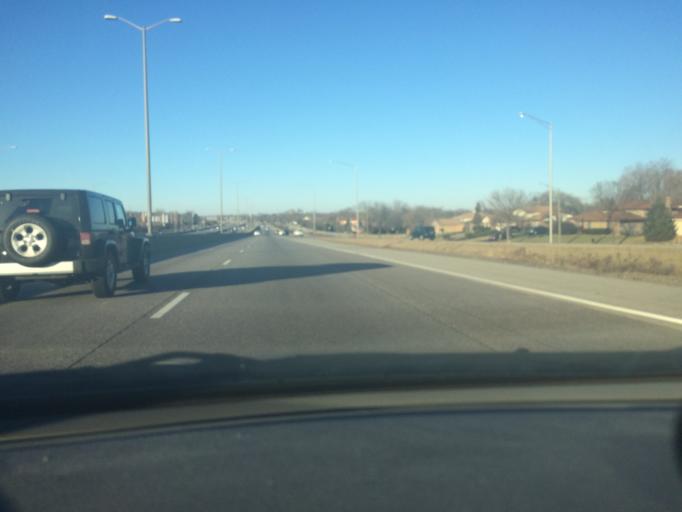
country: US
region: Illinois
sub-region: Cook County
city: Rolling Meadows
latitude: 42.0645
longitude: -88.0277
